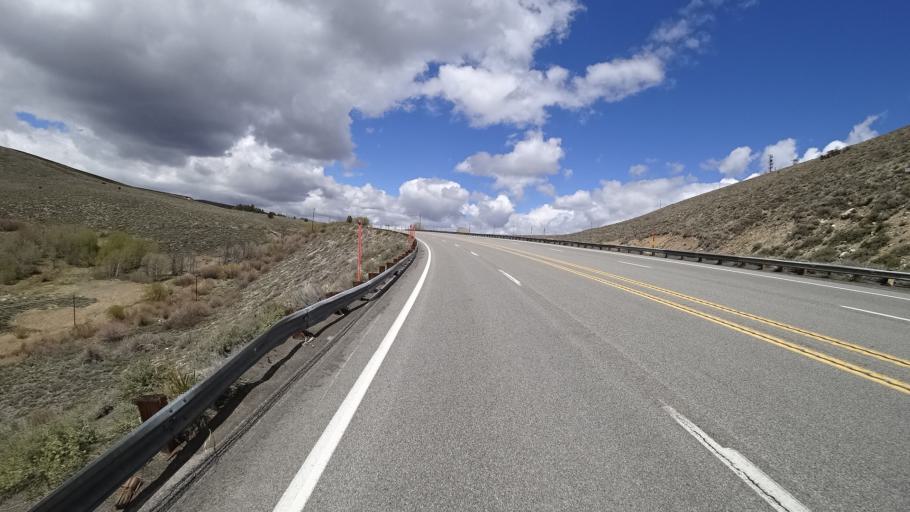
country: US
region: California
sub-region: Mono County
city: Bridgeport
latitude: 38.0839
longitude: -119.1791
